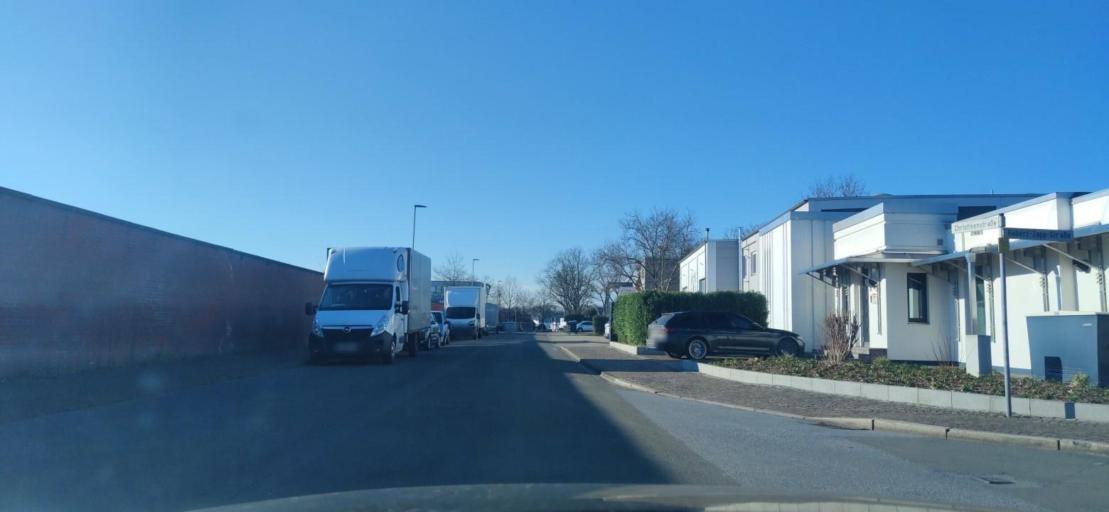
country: DE
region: North Rhine-Westphalia
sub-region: Regierungsbezirk Dusseldorf
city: Ratingen
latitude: 51.3054
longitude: 6.8244
